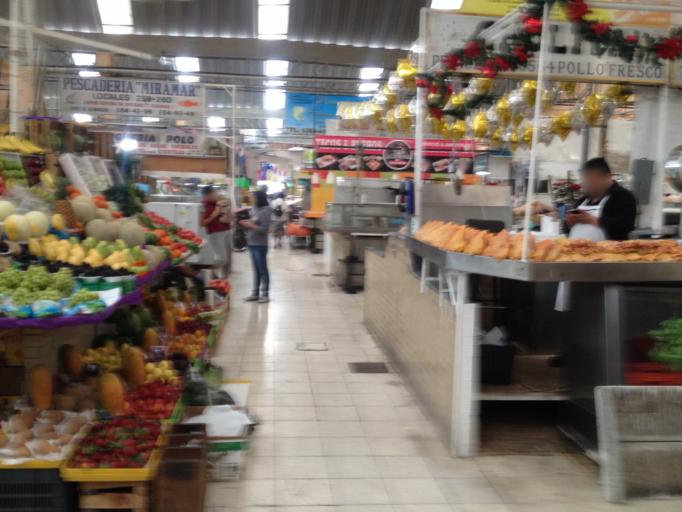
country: MX
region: Mexico City
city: Benito Juarez
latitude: 19.4104
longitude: -99.1633
